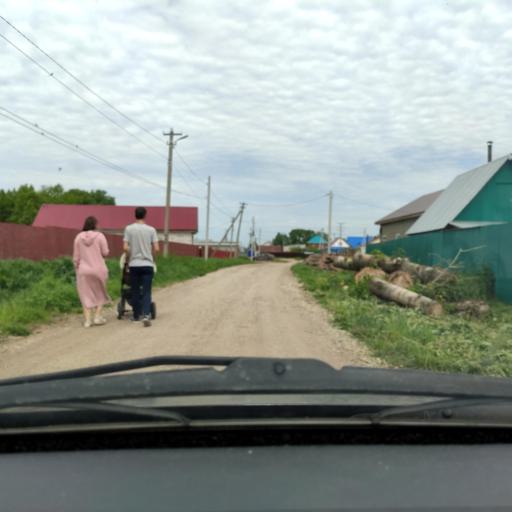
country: RU
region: Bashkortostan
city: Mikhaylovka
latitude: 54.7759
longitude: 55.8216
